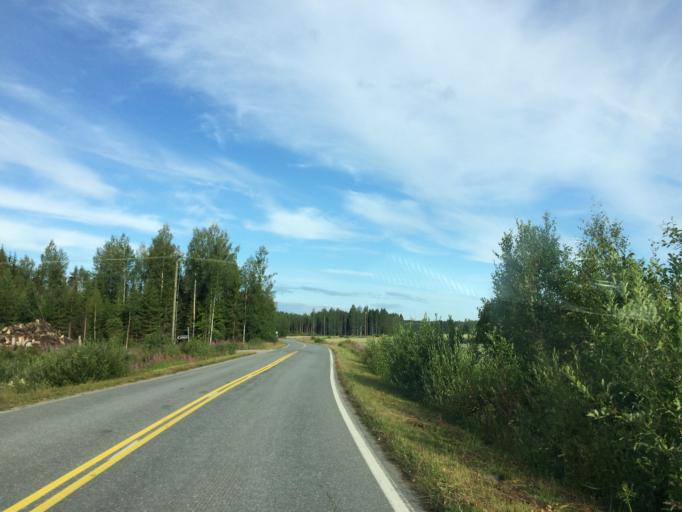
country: FI
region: Haeme
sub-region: Haemeenlinna
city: Janakkala
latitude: 60.9303
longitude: 24.5536
